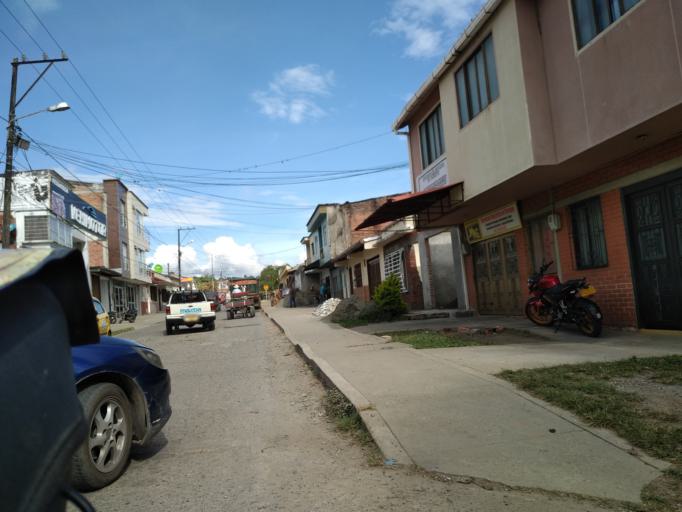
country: CO
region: Valle del Cauca
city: Caicedonia
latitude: 4.3307
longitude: -75.8246
